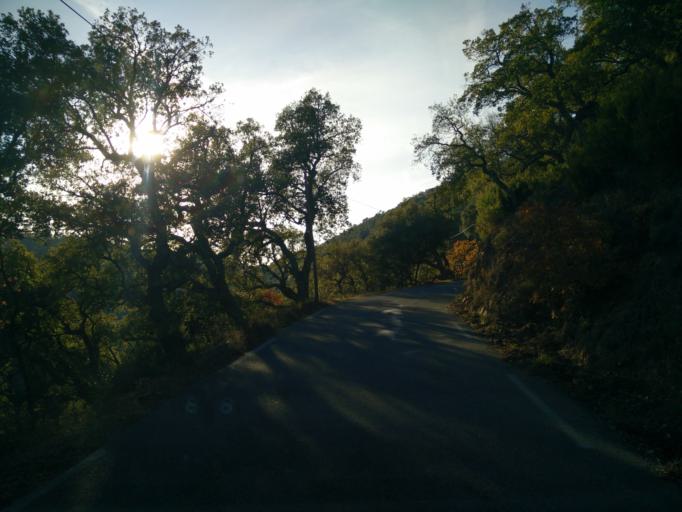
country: FR
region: Provence-Alpes-Cote d'Azur
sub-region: Departement du Var
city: La Garde-Freinet
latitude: 43.3373
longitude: 6.5041
